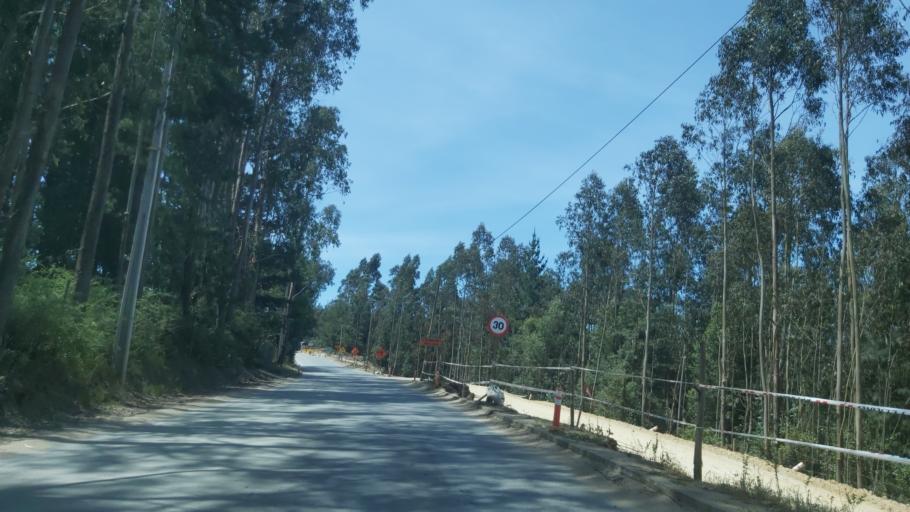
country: CL
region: Maule
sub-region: Provincia de Talca
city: Constitucion
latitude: -35.4404
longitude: -72.4564
